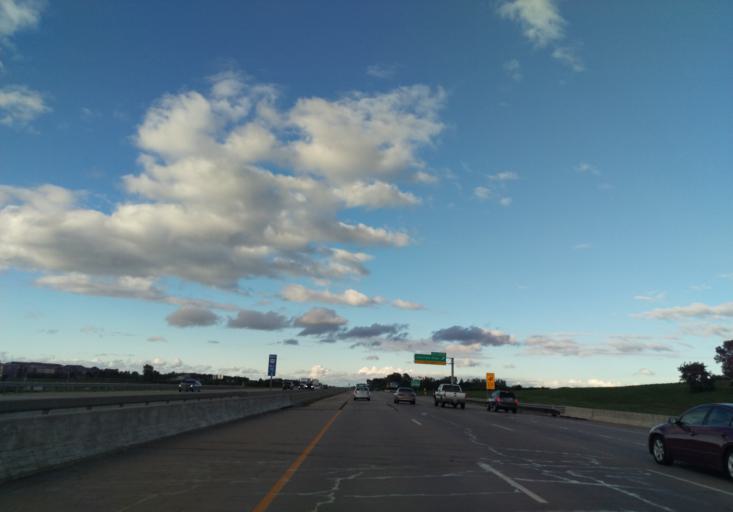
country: US
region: Wisconsin
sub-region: Dane County
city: Sun Prairie
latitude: 43.1454
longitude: -89.2858
